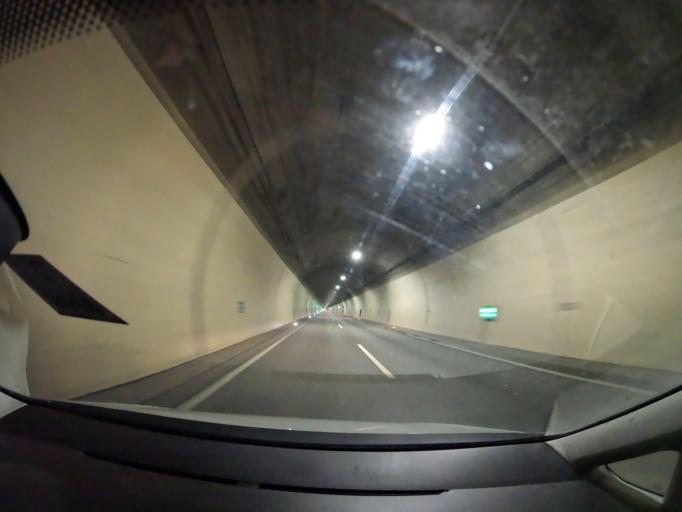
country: AT
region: Carinthia
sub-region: Politischer Bezirk Wolfsberg
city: Bad Sankt Leonhard im Lavanttal
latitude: 46.9055
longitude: 14.8217
